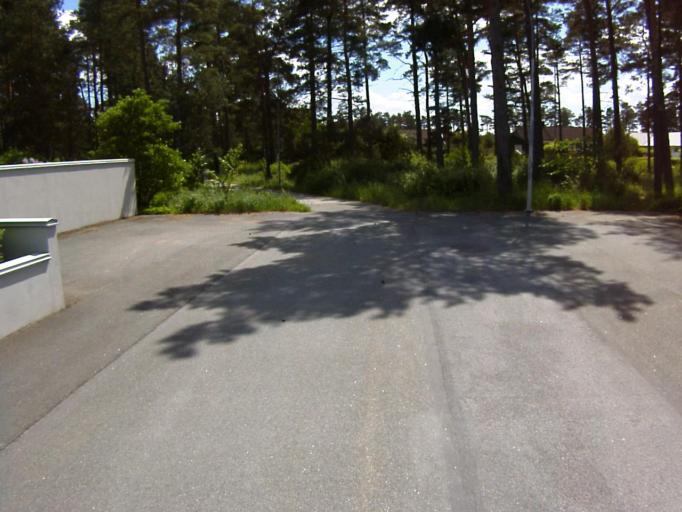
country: SE
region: Skane
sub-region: Kristianstads Kommun
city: Ahus
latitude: 55.9440
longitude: 14.2733
